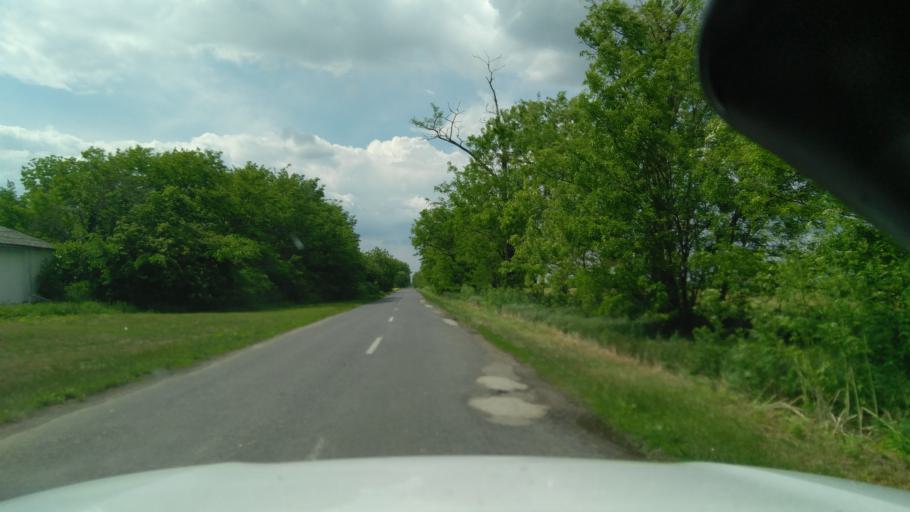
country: HU
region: Bekes
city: Magyarbanhegyes
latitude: 46.4660
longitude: 20.9498
